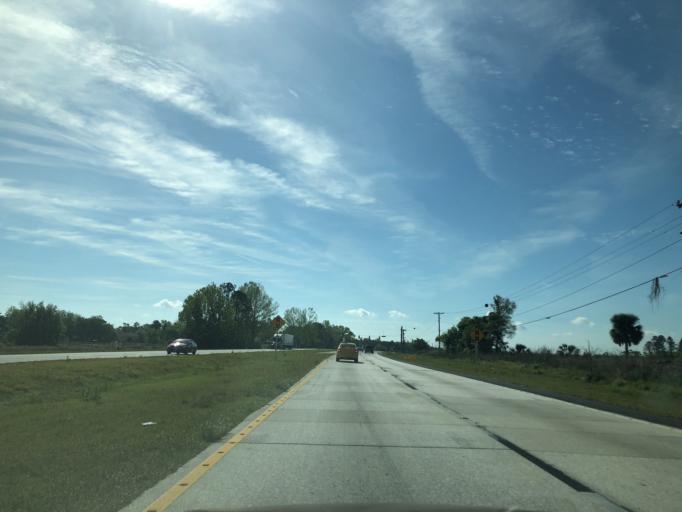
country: US
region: Florida
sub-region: Orange County
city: Zellwood
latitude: 28.7140
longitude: -81.5865
